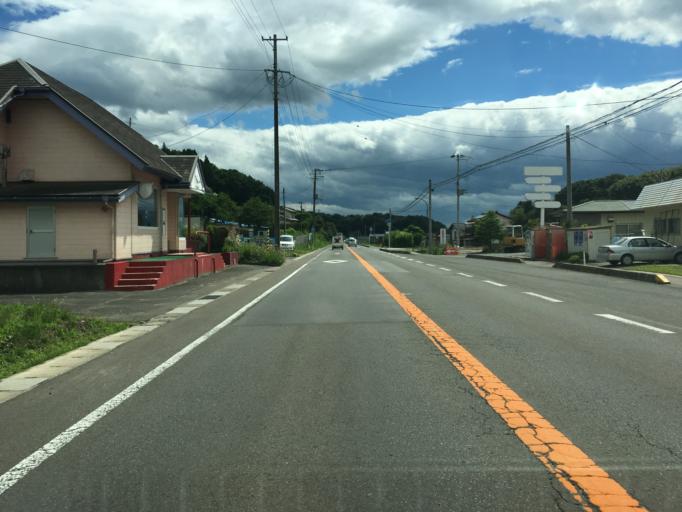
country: JP
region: Fukushima
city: Fukushima-shi
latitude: 37.6716
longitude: 140.5584
